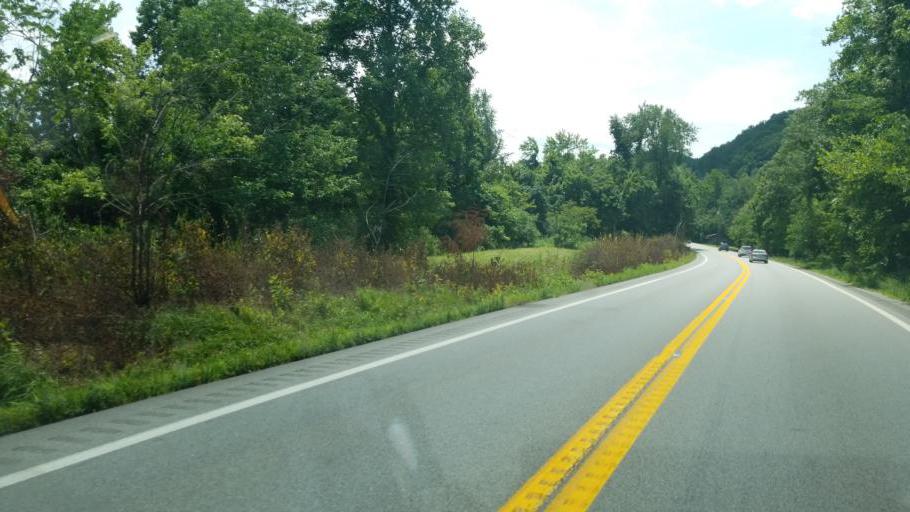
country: US
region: West Virginia
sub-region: Putnam County
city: Buffalo
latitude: 38.6082
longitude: -81.9986
